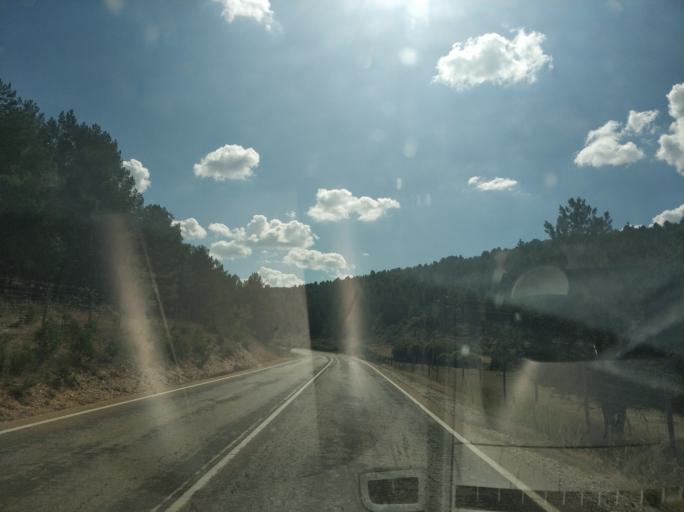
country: ES
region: Castille and Leon
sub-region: Provincia de Soria
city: San Leonardo de Yague
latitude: 41.8159
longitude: -3.0666
